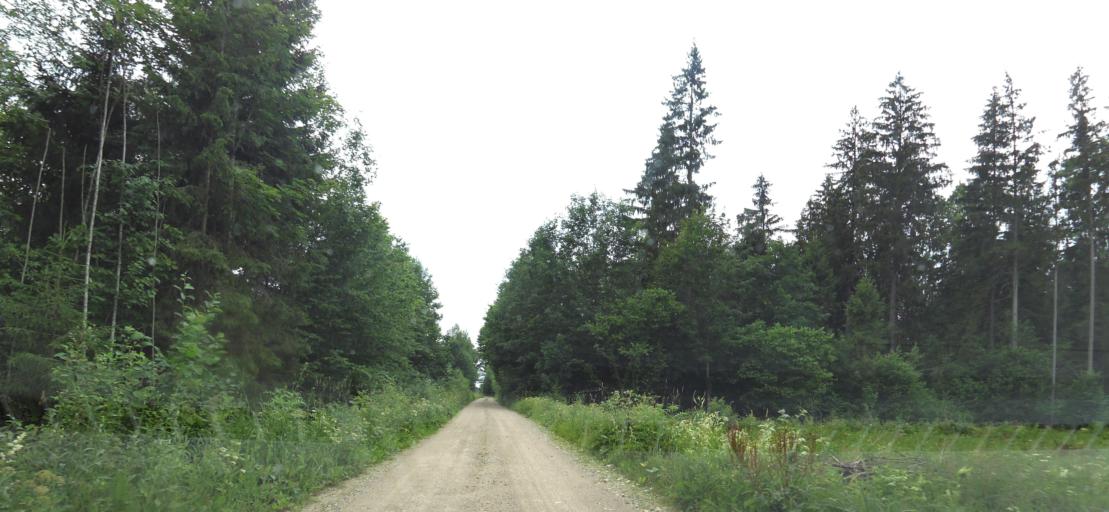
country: LT
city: Obeliai
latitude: 56.1881
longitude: 25.0617
